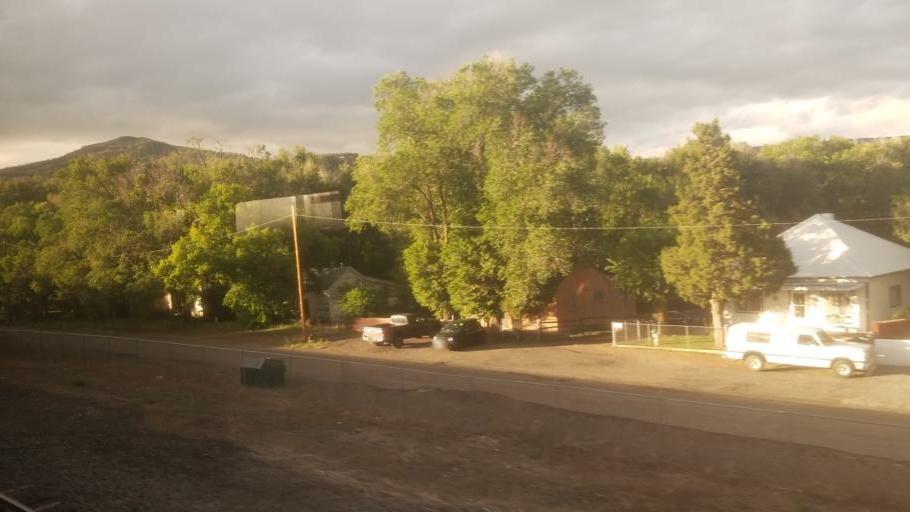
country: US
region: New Mexico
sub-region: Colfax County
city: Raton
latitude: 36.9078
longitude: -104.4398
